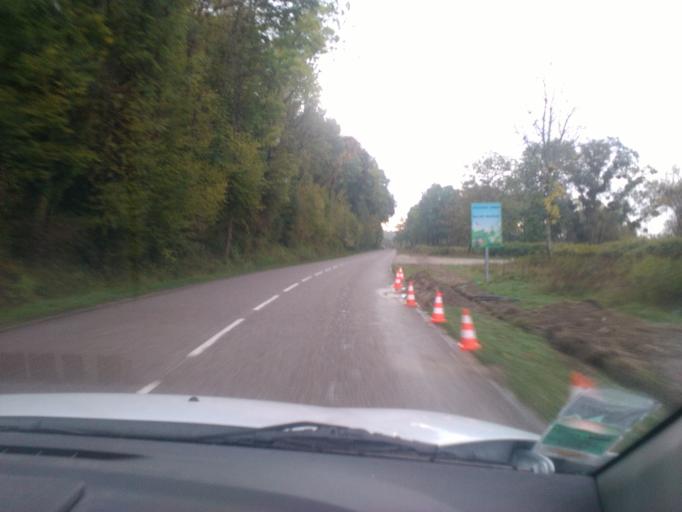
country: FR
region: Lorraine
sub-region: Departement des Vosges
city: Chatel-sur-Moselle
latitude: 48.3108
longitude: 6.3985
